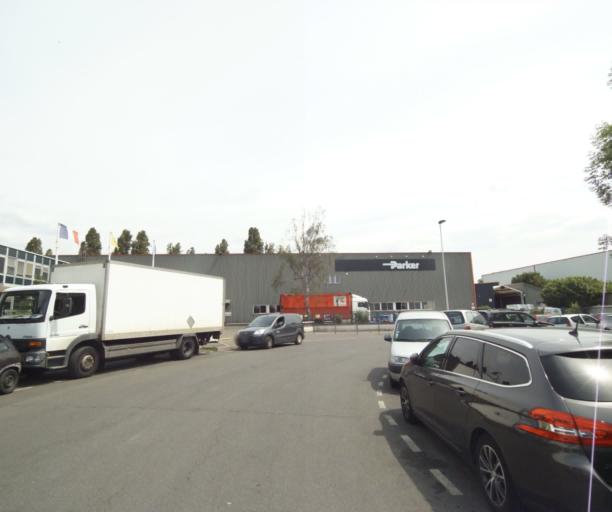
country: FR
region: Ile-de-France
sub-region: Departement du Val-d'Oise
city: Bezons
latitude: 48.9222
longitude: 2.2288
